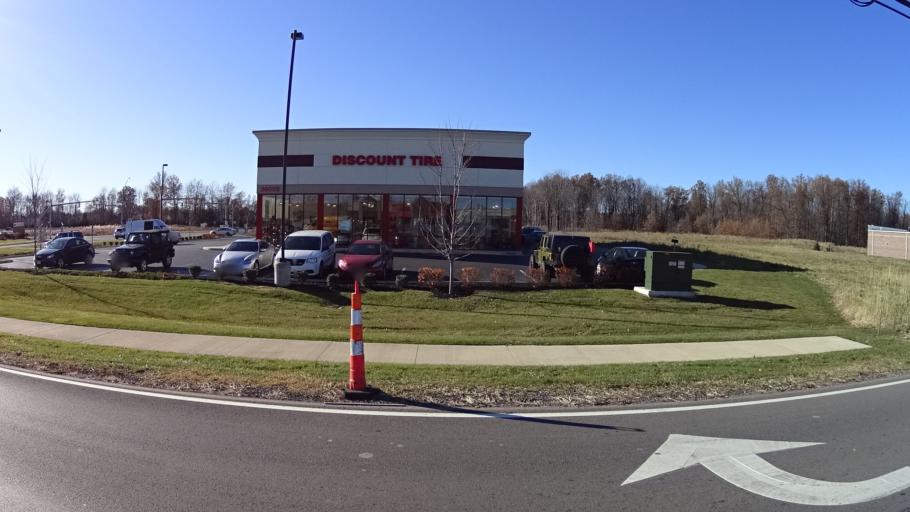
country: US
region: Ohio
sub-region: Lorain County
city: Avon Center
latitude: 41.4704
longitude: -82.0196
